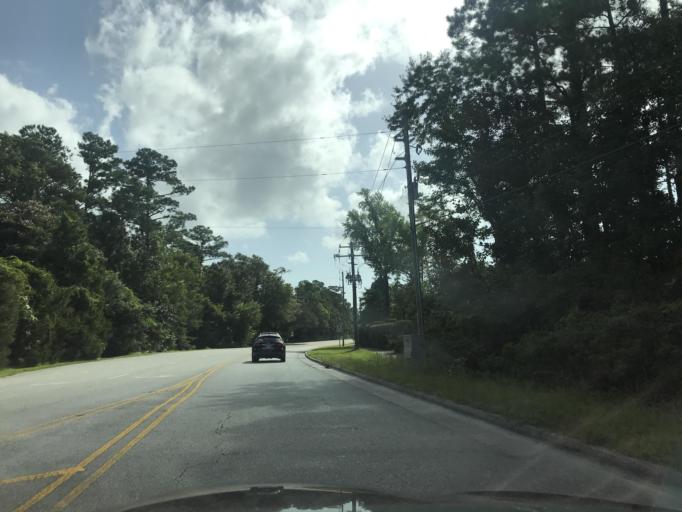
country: US
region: North Carolina
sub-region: New Hanover County
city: Seagate
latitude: 34.2204
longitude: -77.8308
